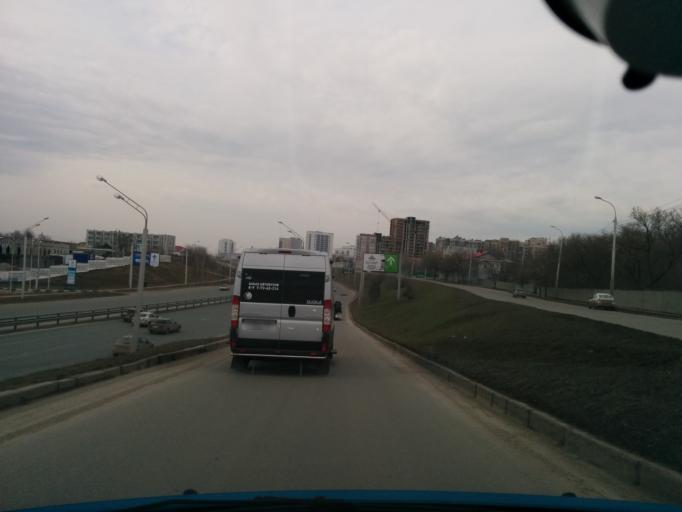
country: RU
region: Bashkortostan
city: Ufa
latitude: 54.7190
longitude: 55.9675
